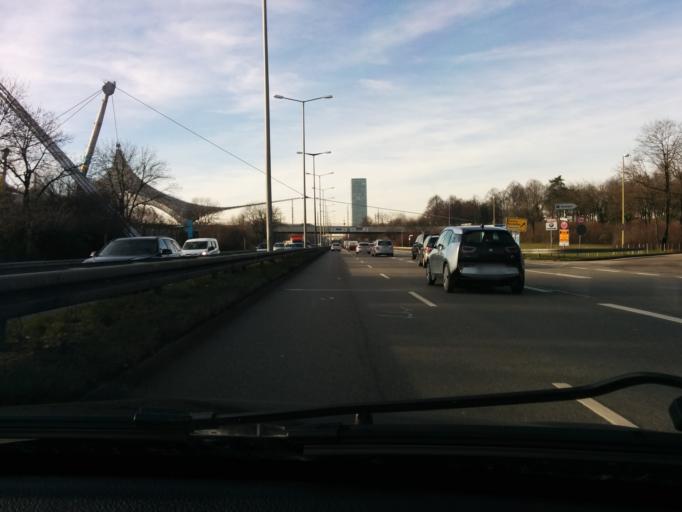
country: DE
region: Bavaria
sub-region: Upper Bavaria
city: Munich
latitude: 48.1762
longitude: 11.5512
